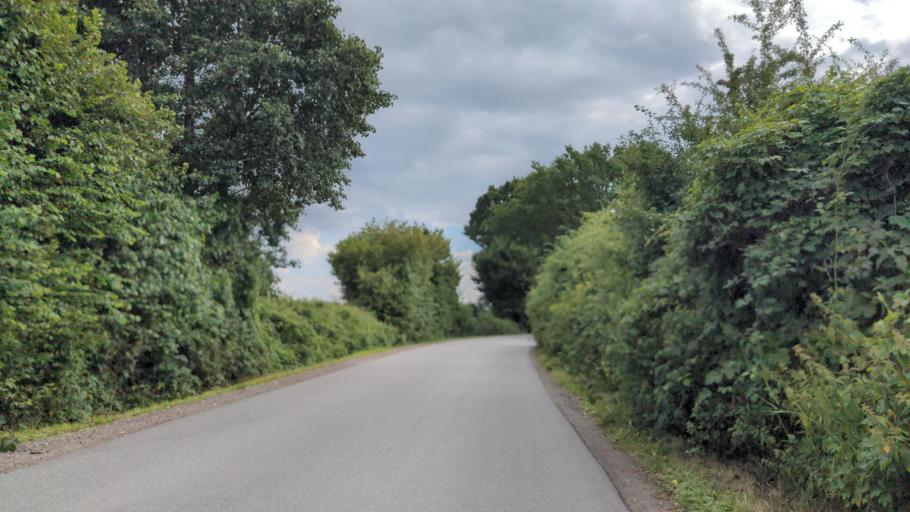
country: DE
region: Schleswig-Holstein
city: Dahme
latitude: 54.2084
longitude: 11.0811
